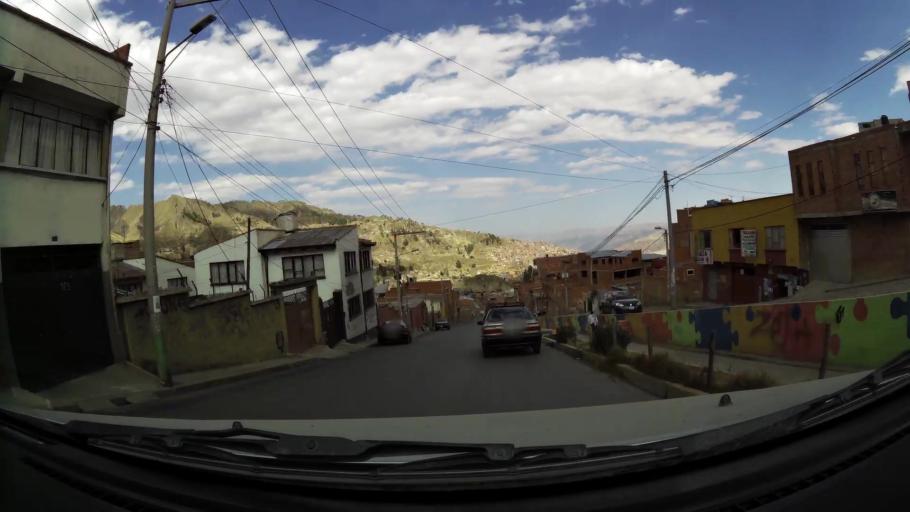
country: BO
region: La Paz
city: La Paz
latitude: -16.4701
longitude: -68.1220
